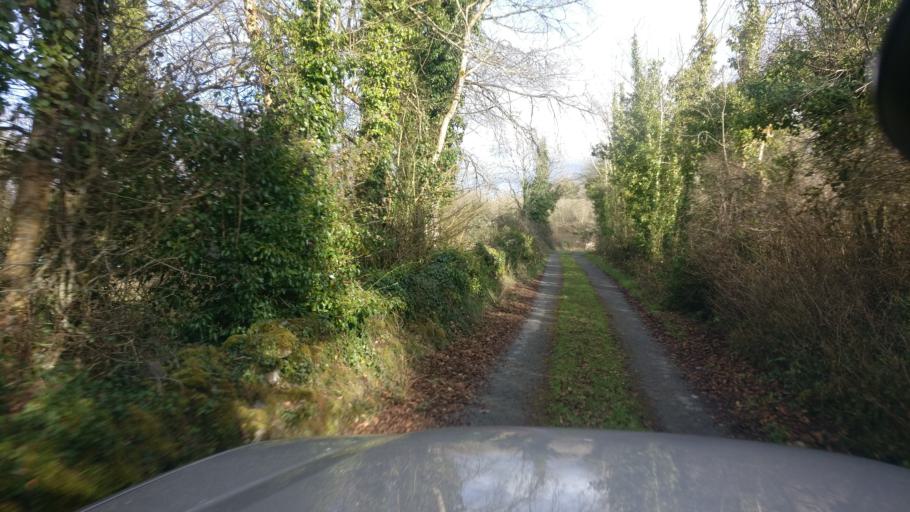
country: IE
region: Connaught
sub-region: County Galway
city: Loughrea
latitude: 53.1822
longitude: -8.4253
